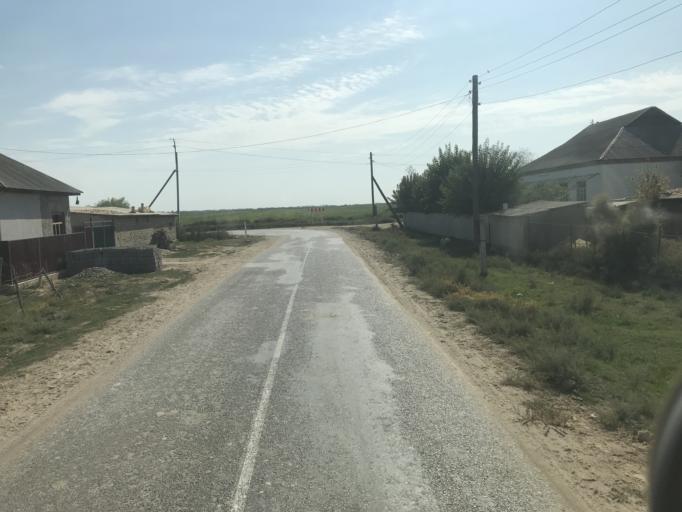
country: KZ
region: Ongtustik Qazaqstan
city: Myrzakent
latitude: 40.6641
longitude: 68.6322
